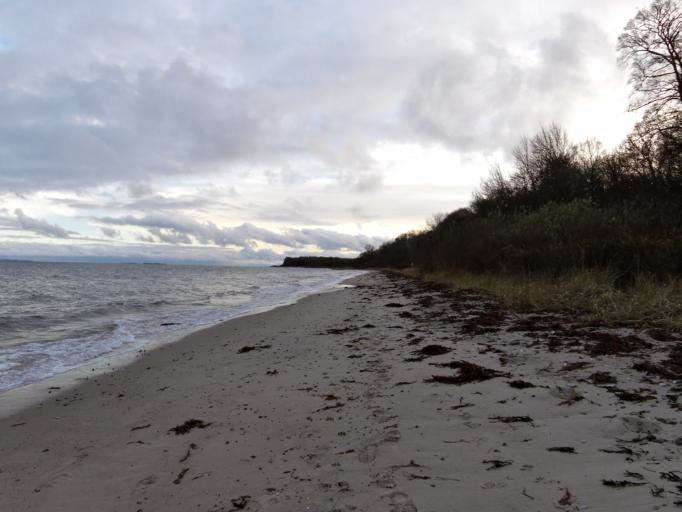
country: DK
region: Central Jutland
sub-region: Arhus Kommune
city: Beder
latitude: 56.0609
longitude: 10.2599
